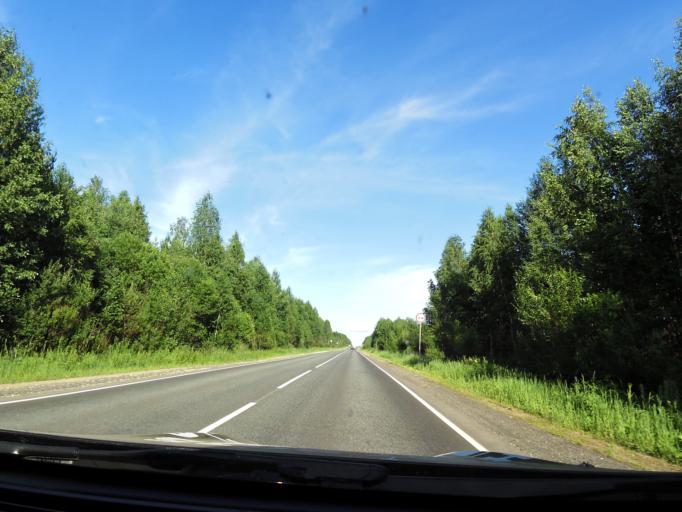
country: RU
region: Kirov
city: Chernaya Kholunitsa
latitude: 58.8710
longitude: 51.5340
